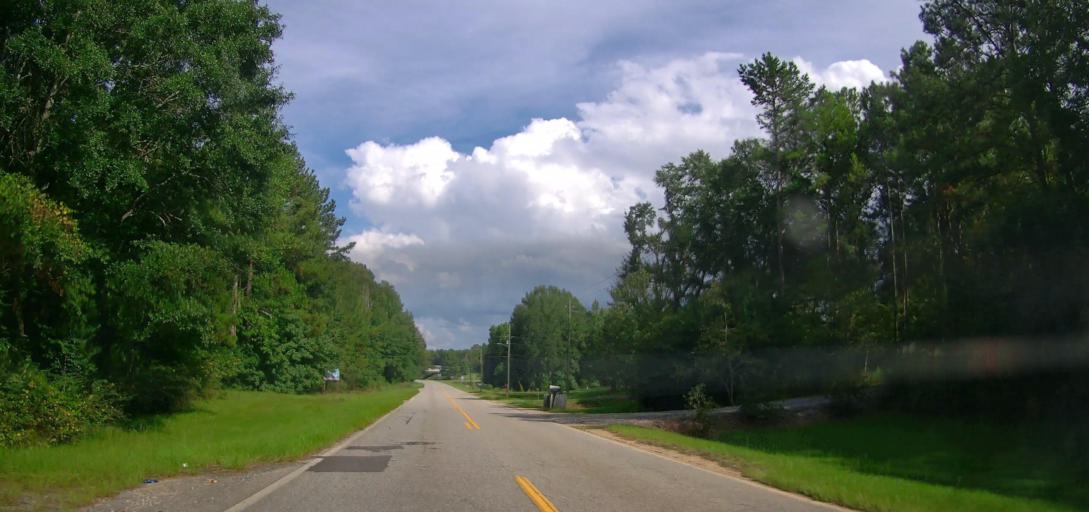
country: US
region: Alabama
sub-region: Russell County
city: Phenix City
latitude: 32.6048
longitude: -84.9568
